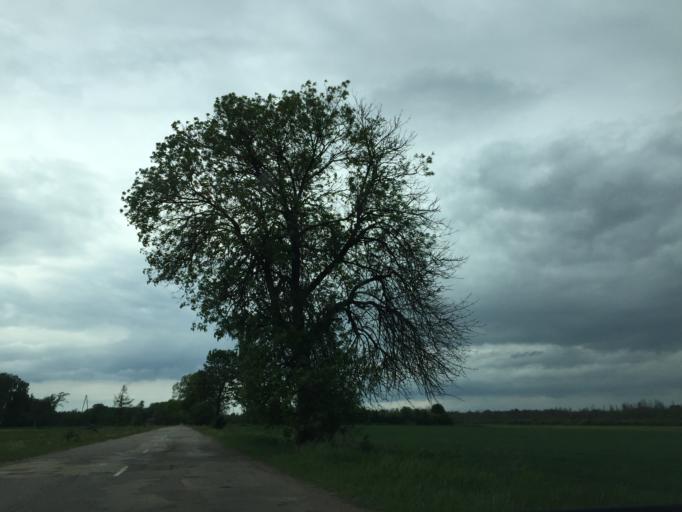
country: LV
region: Preilu Rajons
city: Preili
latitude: 56.0687
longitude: 26.7527
